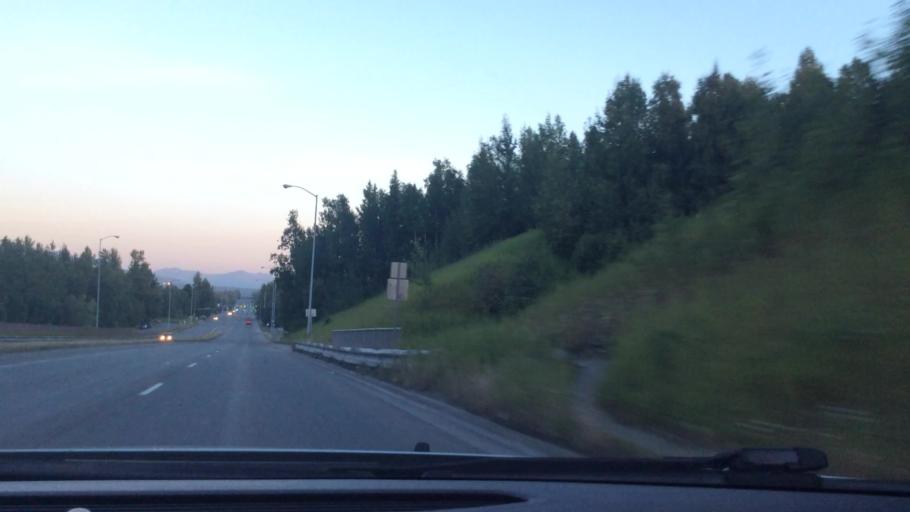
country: US
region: Alaska
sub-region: Anchorage Municipality
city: Anchorage
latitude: 61.2032
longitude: -149.7786
